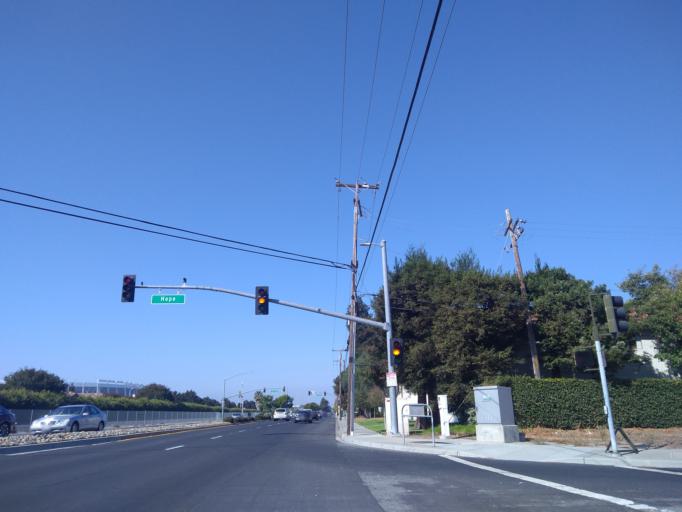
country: US
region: California
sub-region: Santa Clara County
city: Santa Clara
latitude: 37.3977
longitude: -121.9604
